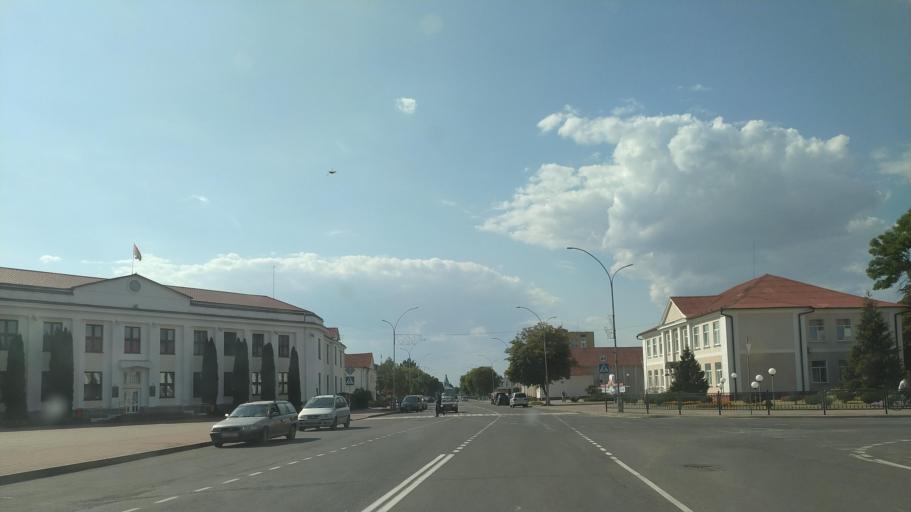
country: BY
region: Brest
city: Drahichyn
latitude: 52.1857
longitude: 25.1605
